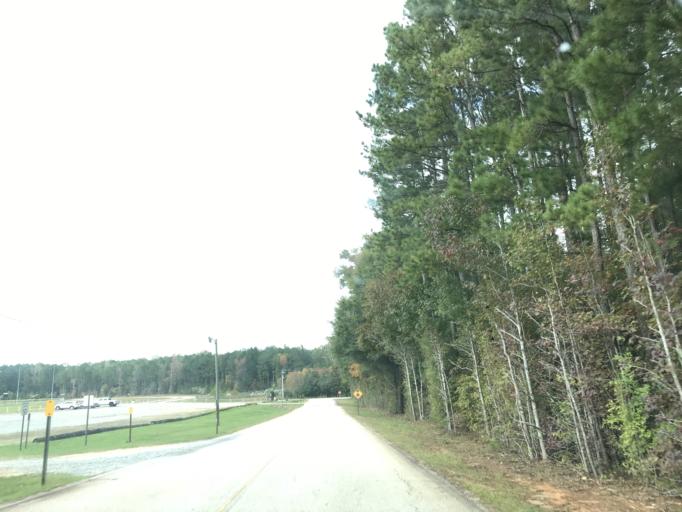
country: US
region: Georgia
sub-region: Jones County
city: Gray
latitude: 32.9867
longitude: -83.5204
